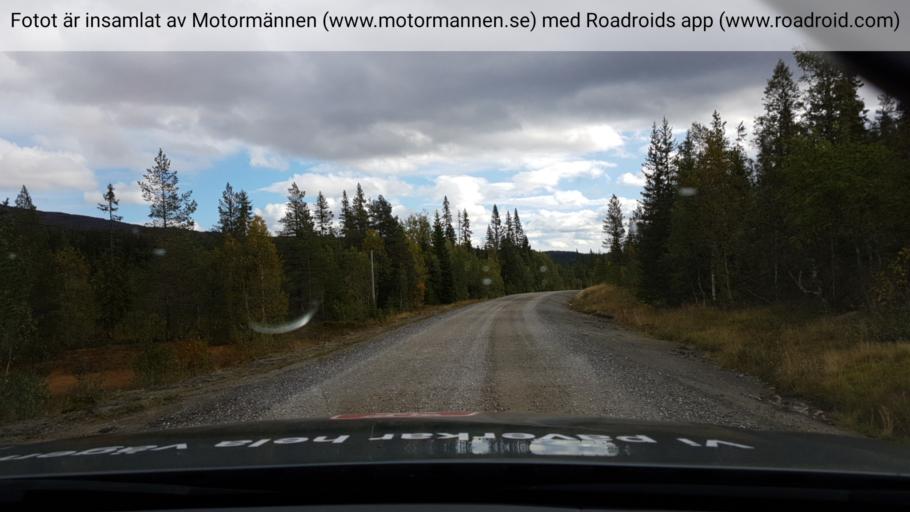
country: NO
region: Nord-Trondelag
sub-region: Snasa
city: Snaase
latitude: 63.7247
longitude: 12.5994
